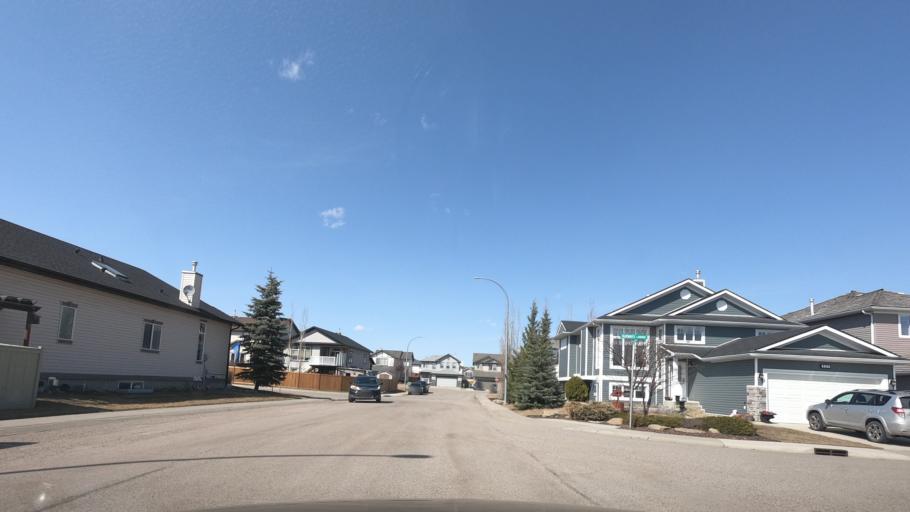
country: CA
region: Alberta
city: Airdrie
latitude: 51.2978
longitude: -114.0468
